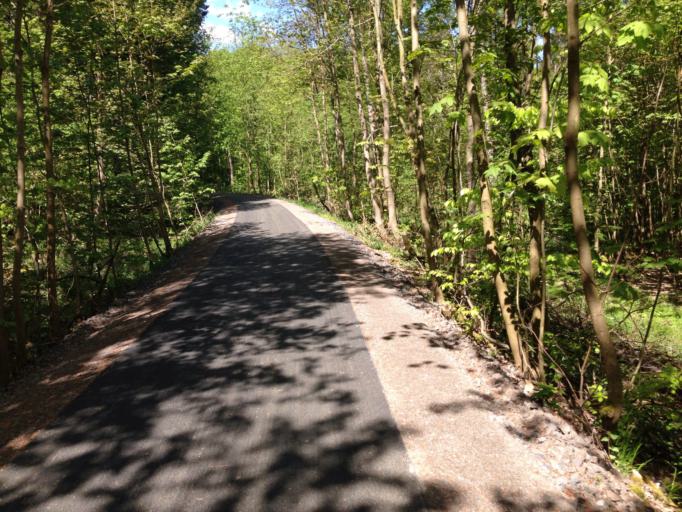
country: DE
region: Hesse
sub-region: Regierungsbezirk Giessen
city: Laubach
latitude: 50.5309
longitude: 8.9498
